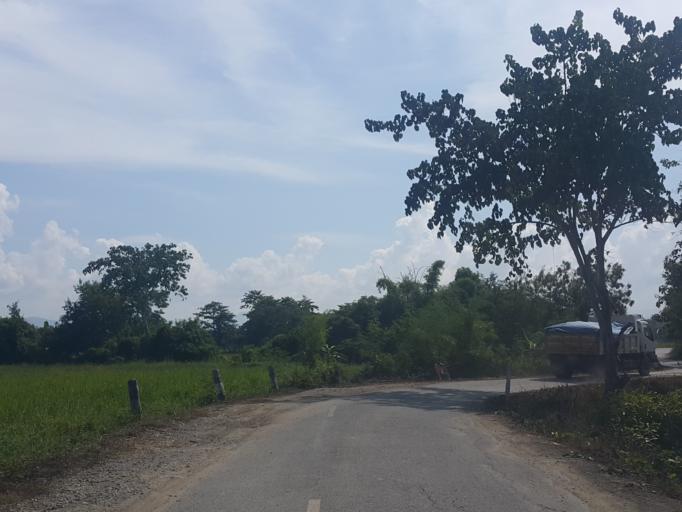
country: TH
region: Chiang Mai
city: San Kamphaeng
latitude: 18.7728
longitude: 99.1040
